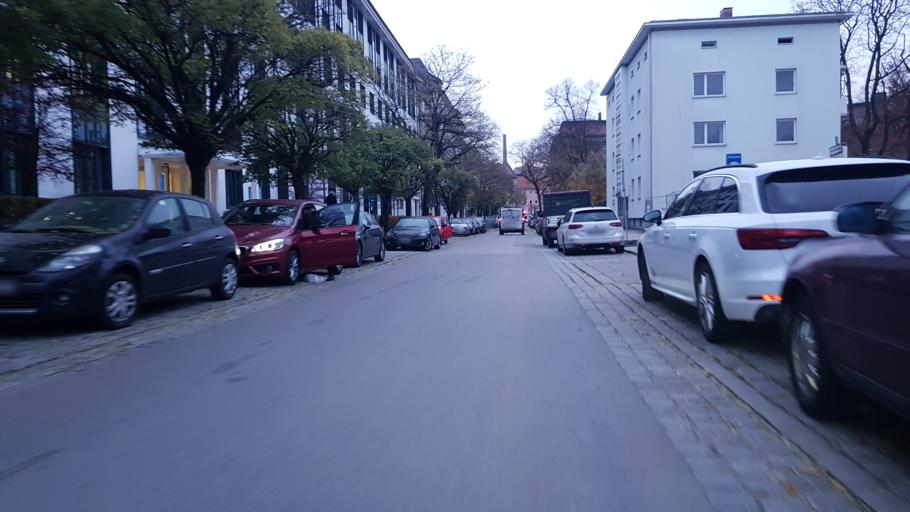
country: DE
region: Bavaria
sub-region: Upper Bavaria
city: Munich
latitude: 48.1481
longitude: 11.5491
